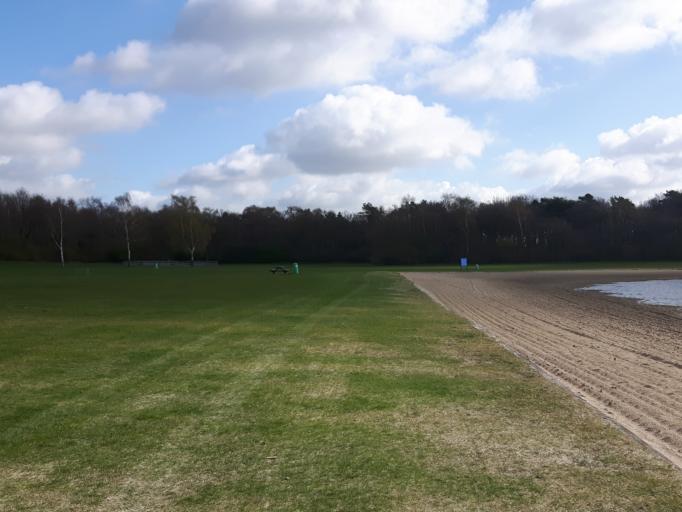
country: NL
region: Overijssel
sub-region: Gemeente Enschede
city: Enschede
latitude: 52.1827
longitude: 6.8411
